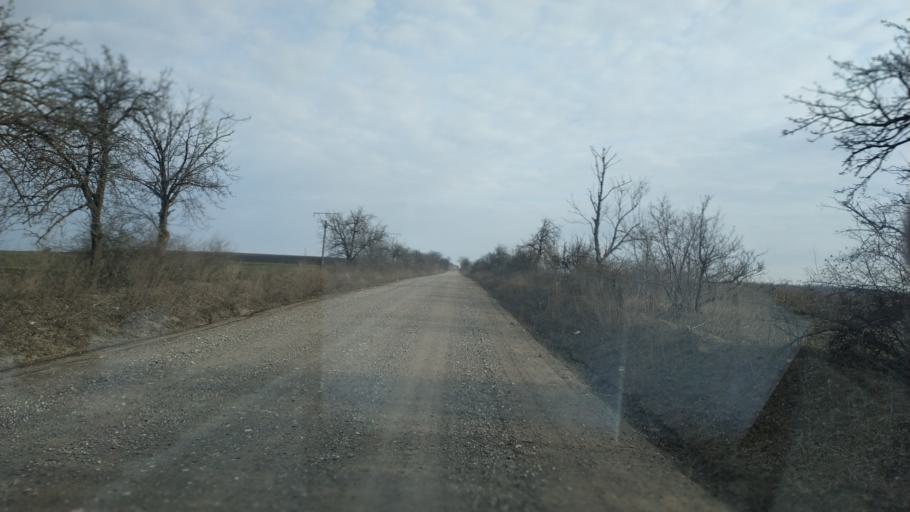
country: MD
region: Chisinau
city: Vadul lui Voda
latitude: 46.9841
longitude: 29.0860
